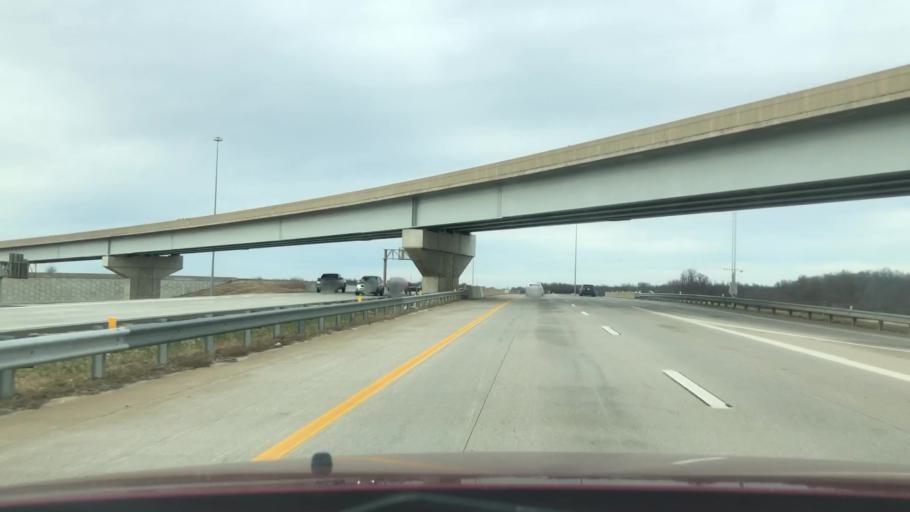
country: US
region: Missouri
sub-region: Greene County
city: Springfield
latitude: 37.2493
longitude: -93.2245
